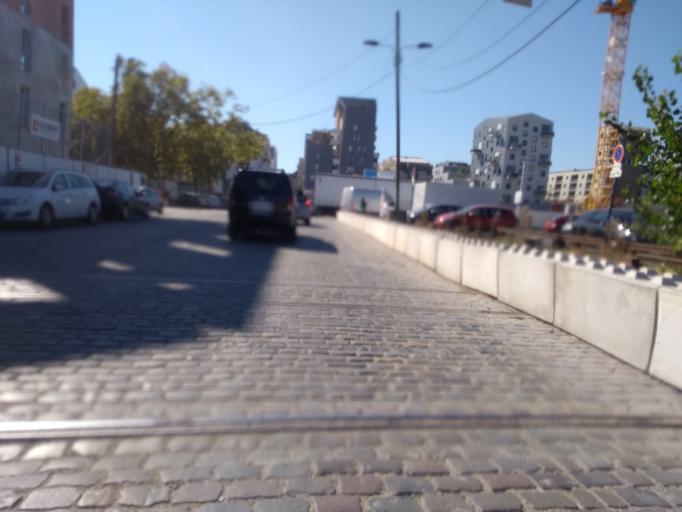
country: FR
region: Aquitaine
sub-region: Departement de la Gironde
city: Bordeaux
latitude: 44.8624
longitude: -0.5542
